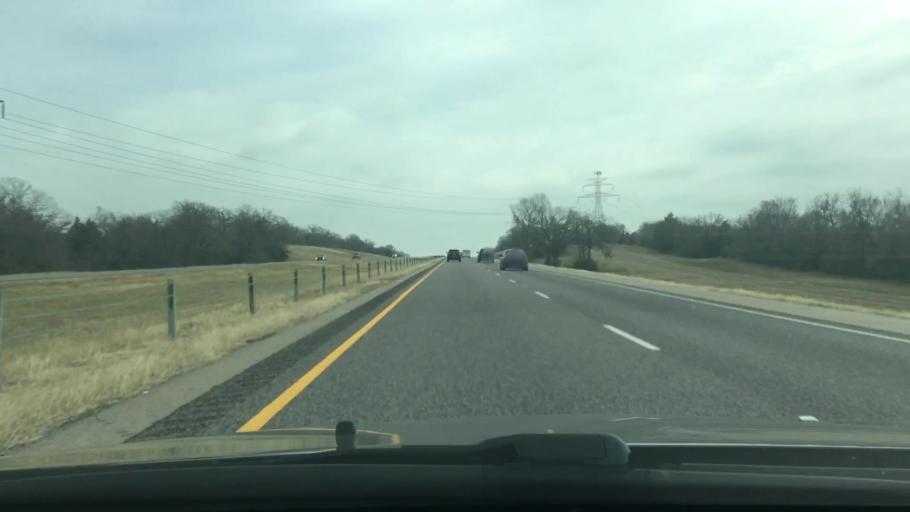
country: US
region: Texas
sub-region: Leon County
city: Buffalo
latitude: 31.5361
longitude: -96.1204
